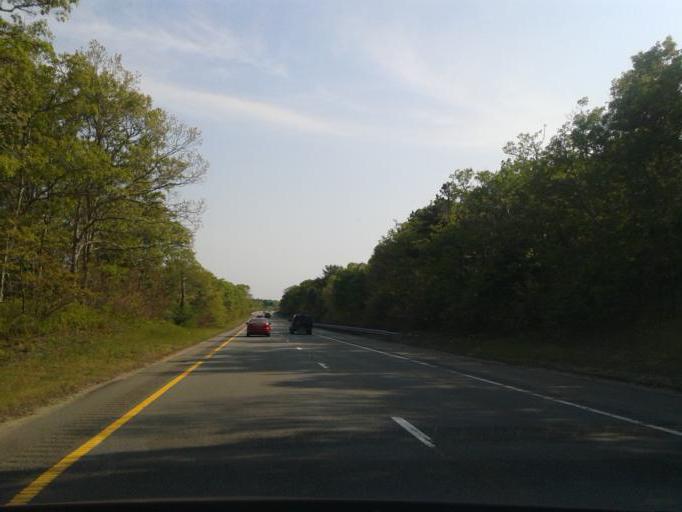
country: US
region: Massachusetts
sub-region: Barnstable County
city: North Falmouth
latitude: 41.6486
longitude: -70.6040
